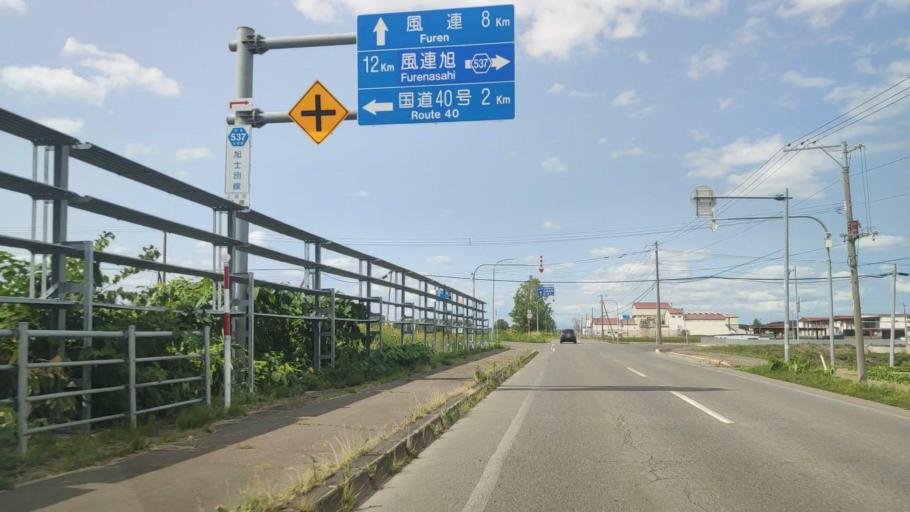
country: JP
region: Hokkaido
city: Nayoro
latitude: 44.2003
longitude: 142.4158
